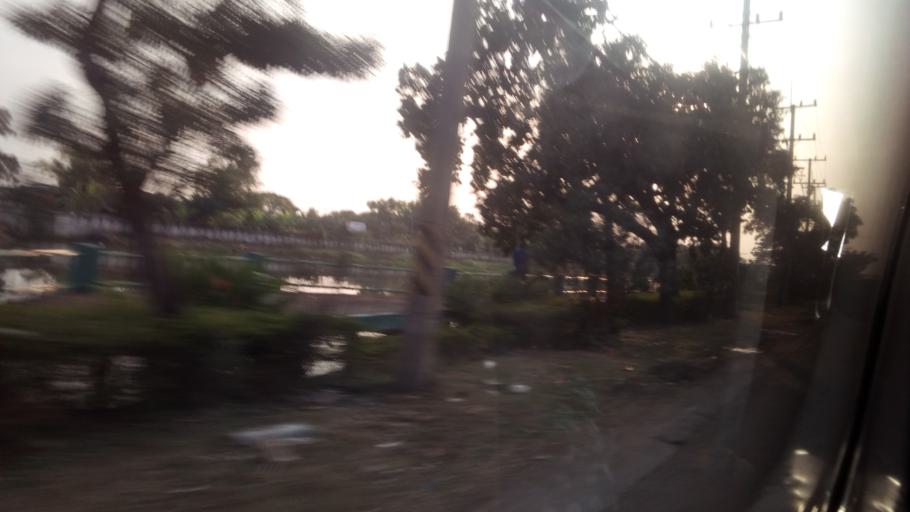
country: TH
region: Pathum Thani
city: Thanyaburi
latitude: 13.9995
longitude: 100.6848
